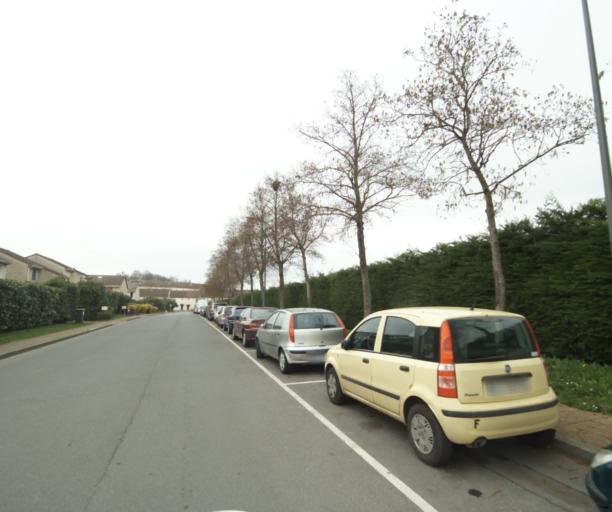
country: FR
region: Ile-de-France
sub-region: Departement du Val-d'Oise
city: Vaureal
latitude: 49.0448
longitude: 2.0289
